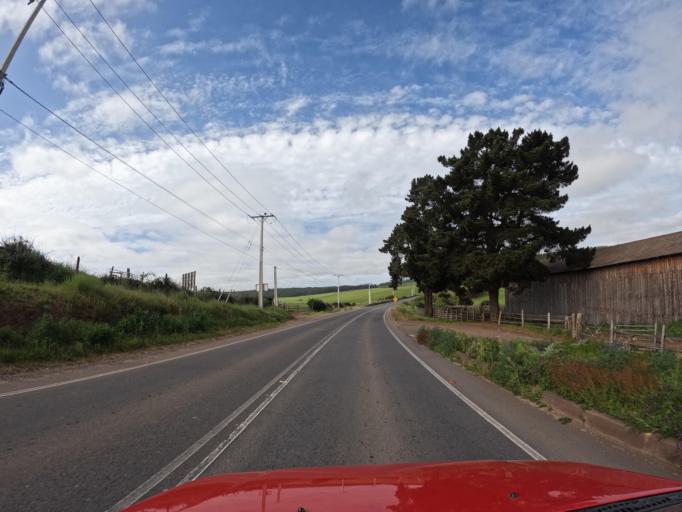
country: CL
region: O'Higgins
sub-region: Provincia de Colchagua
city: Santa Cruz
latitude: -34.3506
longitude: -71.9386
